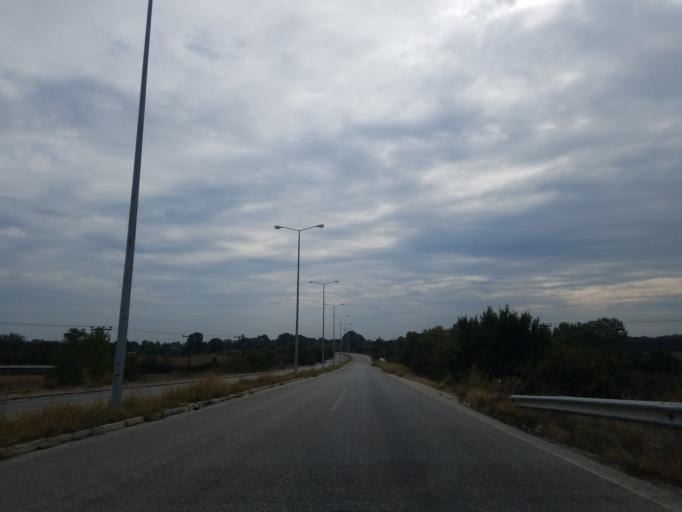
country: GR
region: Thessaly
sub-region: Trikala
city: Pyrgetos
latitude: 39.5196
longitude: 21.7592
